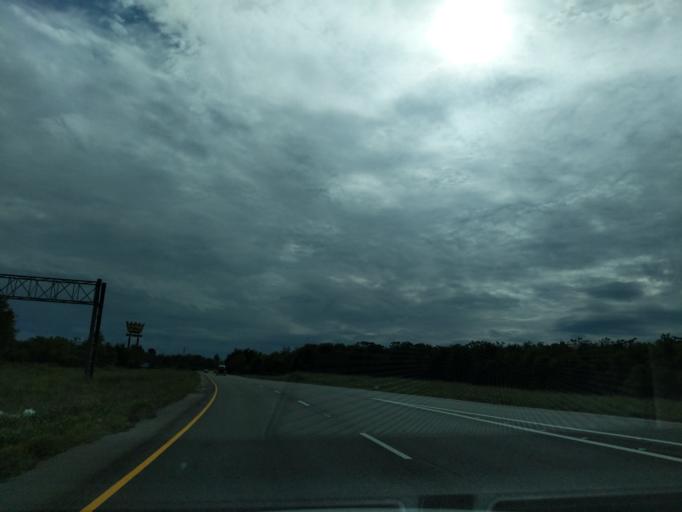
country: US
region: Louisiana
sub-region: Saint Bernard Parish
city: Chalmette
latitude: 30.0161
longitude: -89.9439
